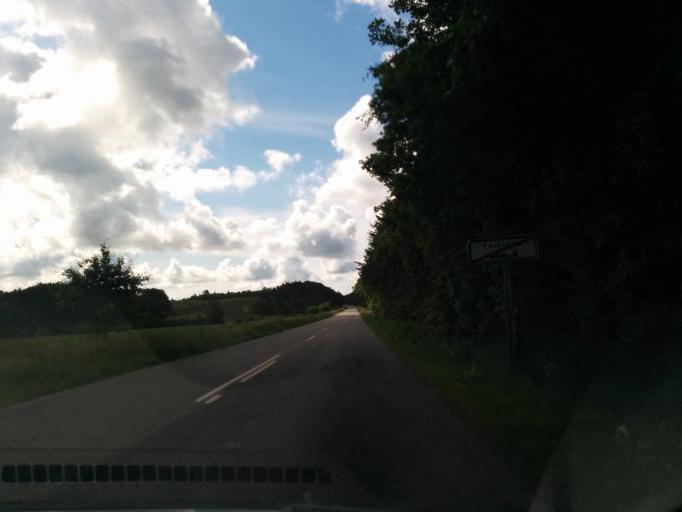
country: DK
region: Central Jutland
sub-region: Syddjurs Kommune
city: Ronde
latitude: 56.2821
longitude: 10.5888
